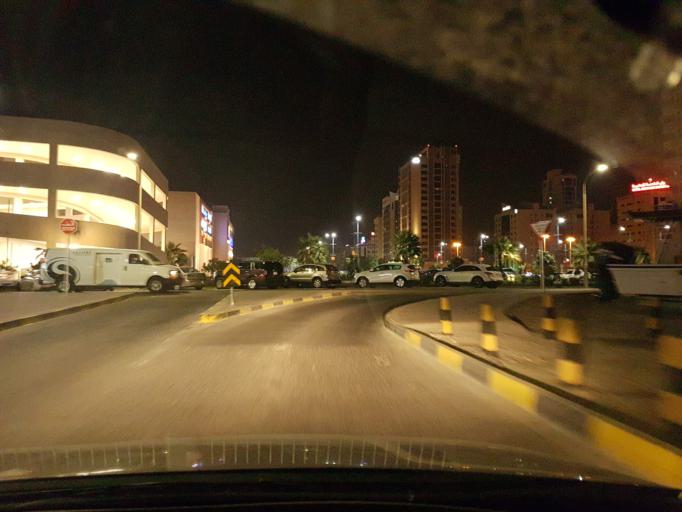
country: BH
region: Manama
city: Manama
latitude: 26.2151
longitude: 50.6002
